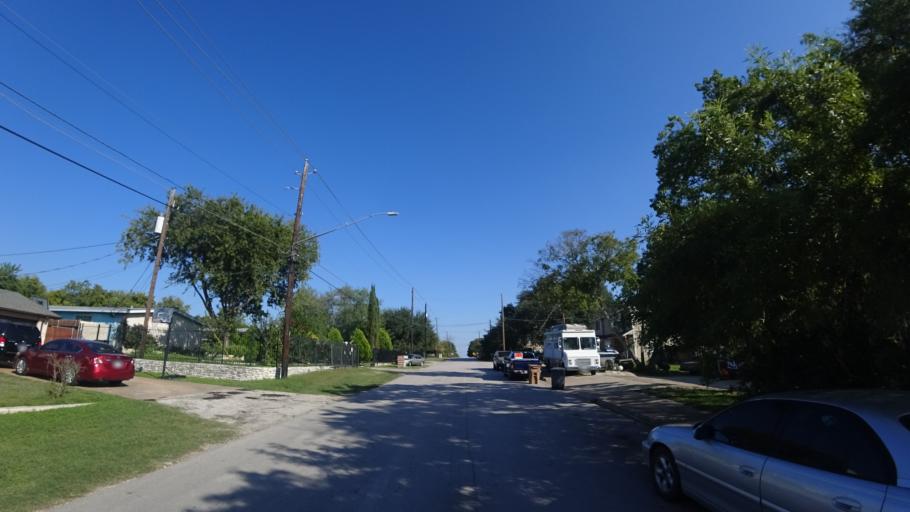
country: US
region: Texas
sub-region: Travis County
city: Wells Branch
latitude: 30.3438
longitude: -97.6750
